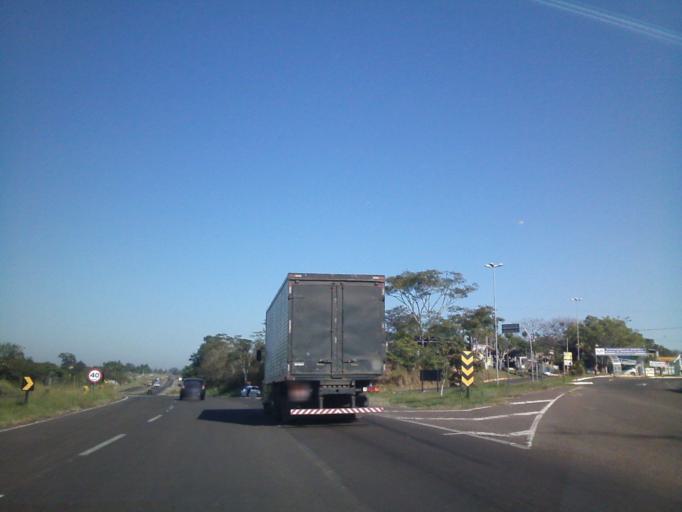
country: BR
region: Sao Paulo
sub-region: Presidente Prudente
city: Presidente Prudente
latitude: -22.1790
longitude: -51.4162
